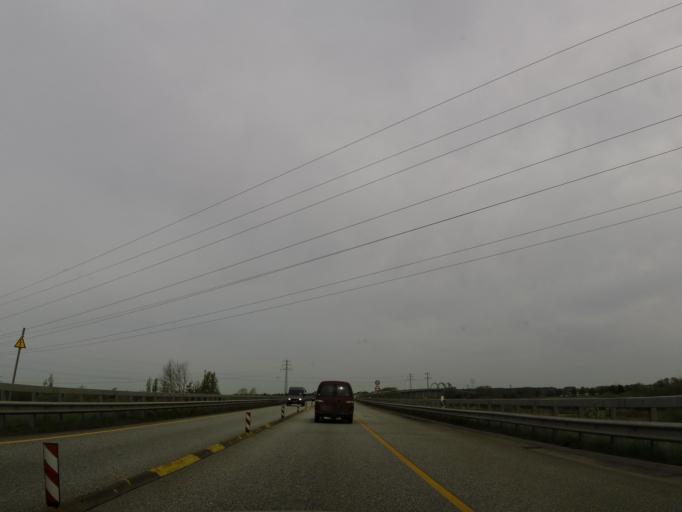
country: DE
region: Schleswig-Holstein
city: Heiligenstedten
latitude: 53.9140
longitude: 9.4828
